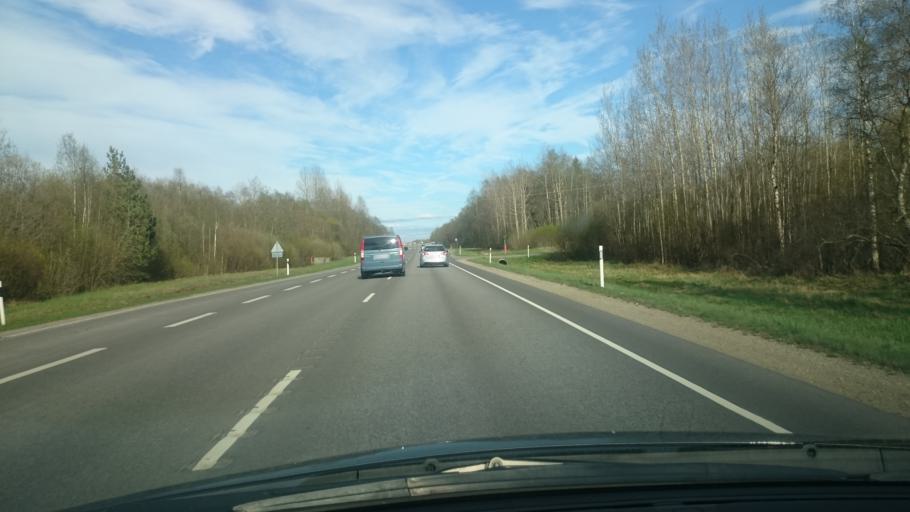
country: EE
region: Ida-Virumaa
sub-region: Sillamaee linn
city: Sillamae
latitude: 59.3916
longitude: 27.7053
